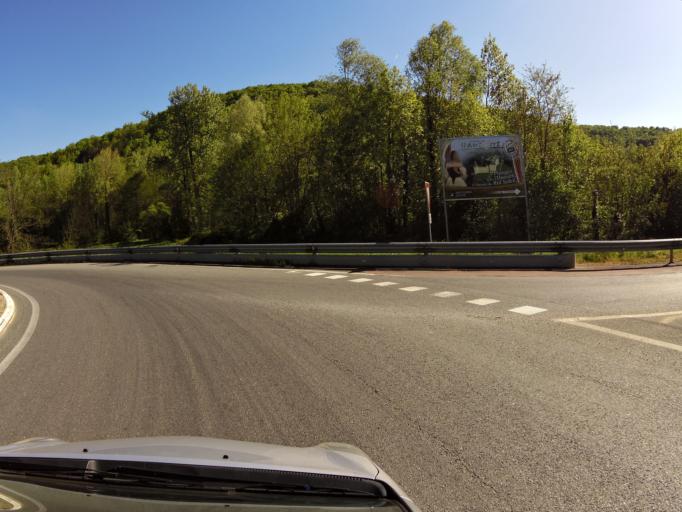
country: FR
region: Aquitaine
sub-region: Departement de la Dordogne
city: Montignac
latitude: 45.1483
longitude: 1.1717
